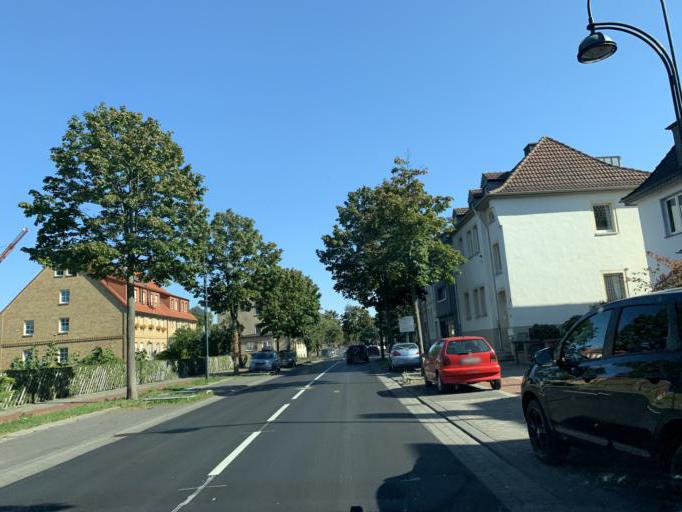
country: DE
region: North Rhine-Westphalia
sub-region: Regierungsbezirk Arnsberg
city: Hamm
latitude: 51.6869
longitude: 7.8454
